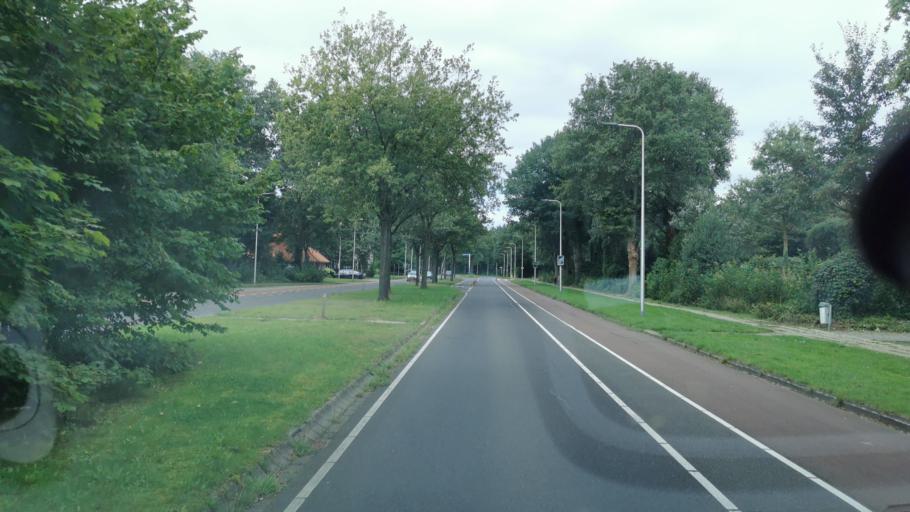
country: NL
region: Overijssel
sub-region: Gemeente Oldenzaal
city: Oldenzaal
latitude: 52.3097
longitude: 6.9044
